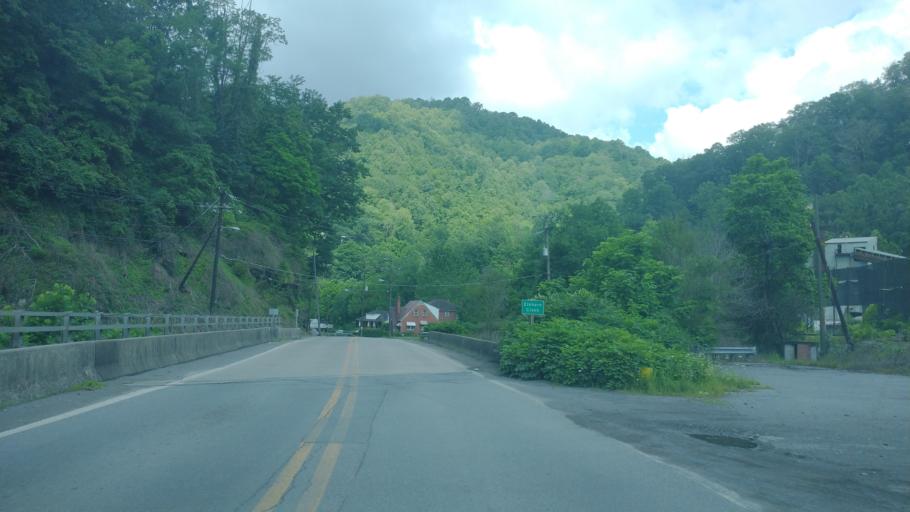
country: US
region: West Virginia
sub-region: McDowell County
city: Welch
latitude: 37.4161
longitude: -81.4480
